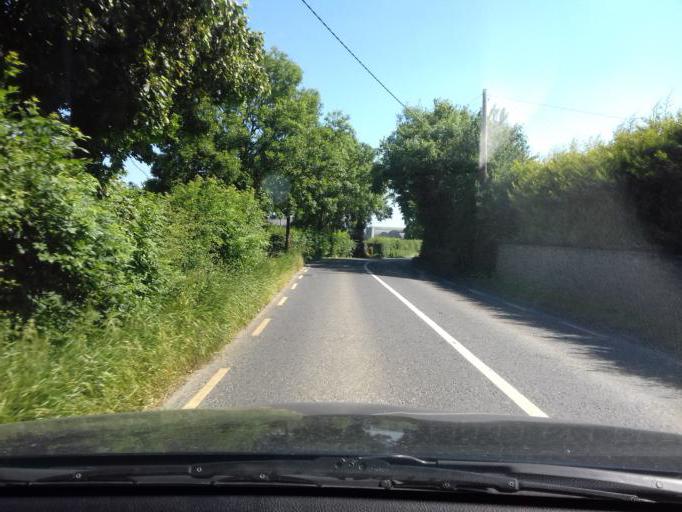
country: IE
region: Leinster
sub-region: Fingal County
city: Swords
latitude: 53.5307
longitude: -6.2699
